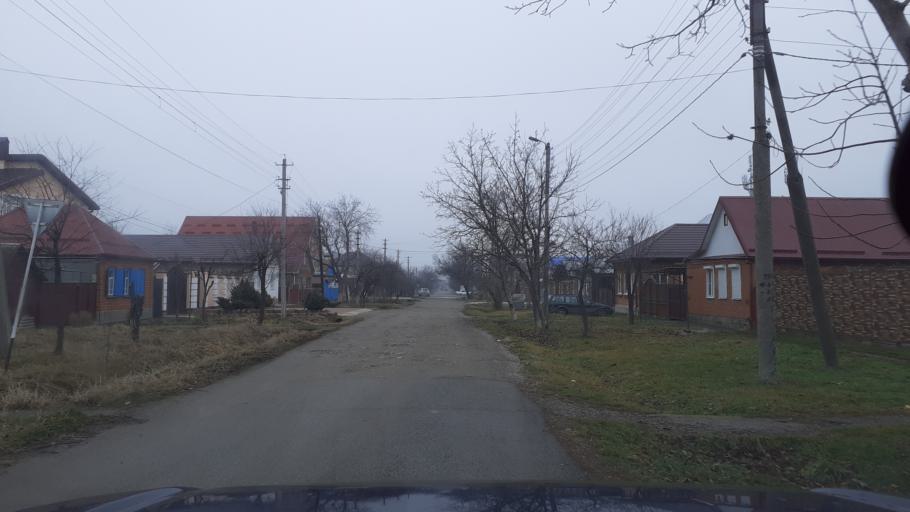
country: RU
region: Adygeya
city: Maykop
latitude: 44.6179
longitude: 40.0880
